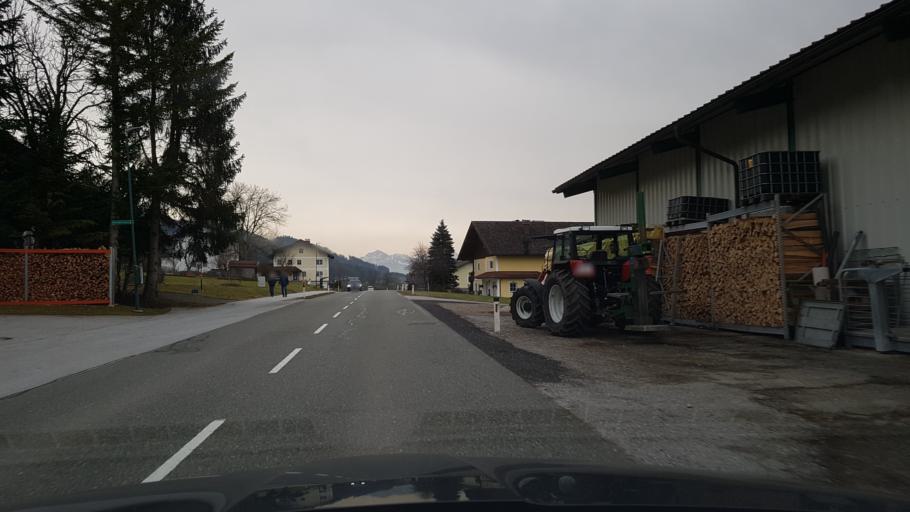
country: AT
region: Salzburg
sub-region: Politischer Bezirk Salzburg-Umgebung
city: Nussdorf am Haunsberg
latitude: 47.9505
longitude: 13.0035
